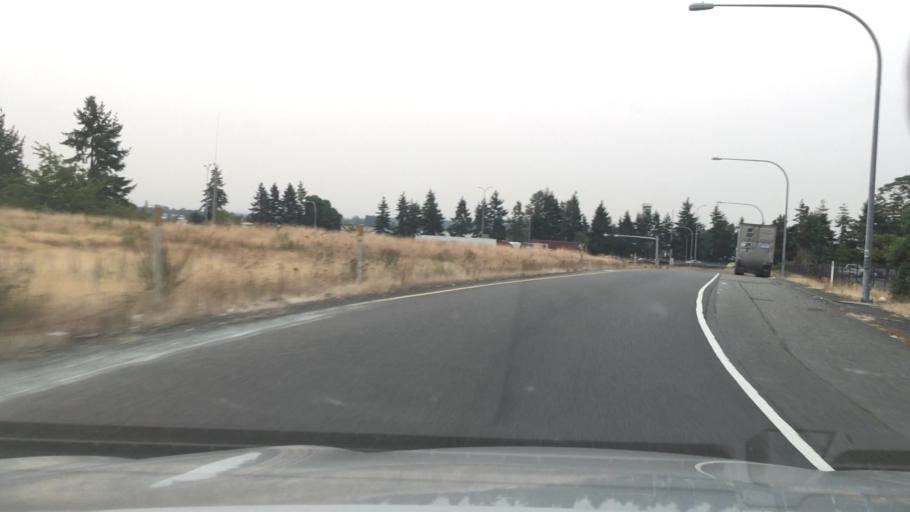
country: US
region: Washington
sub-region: Pierce County
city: McChord Air Force Base
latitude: 47.1635
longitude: -122.4823
